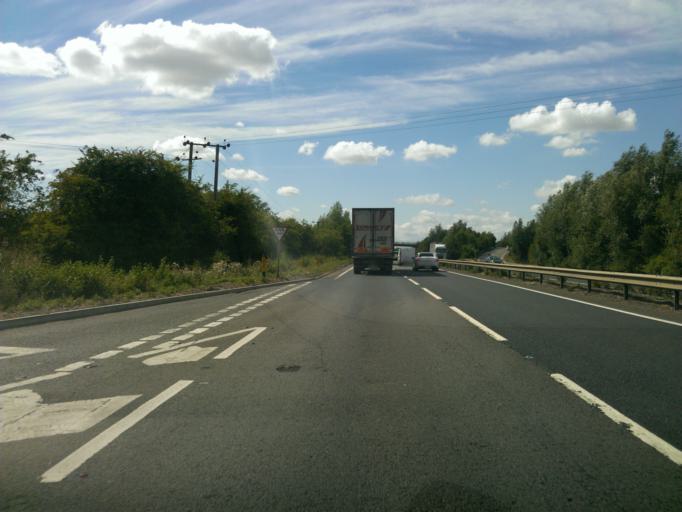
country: GB
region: England
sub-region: Cambridgeshire
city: Buckden
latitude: 52.3337
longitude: -0.2932
